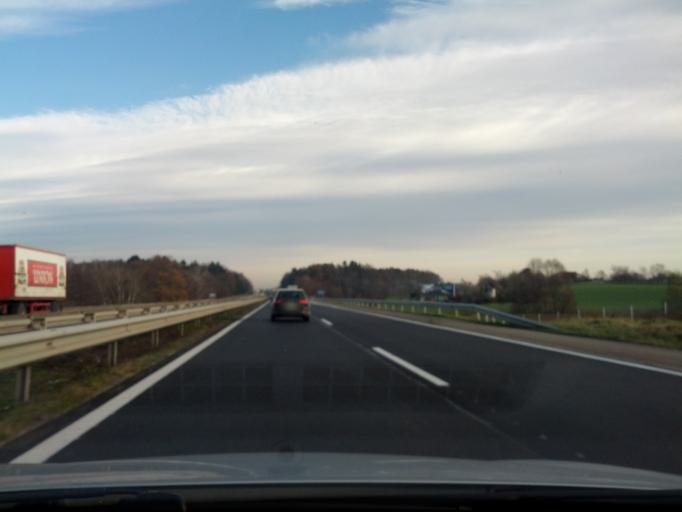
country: SI
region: Race-Fram
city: Morje
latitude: 46.4354
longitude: 15.6397
